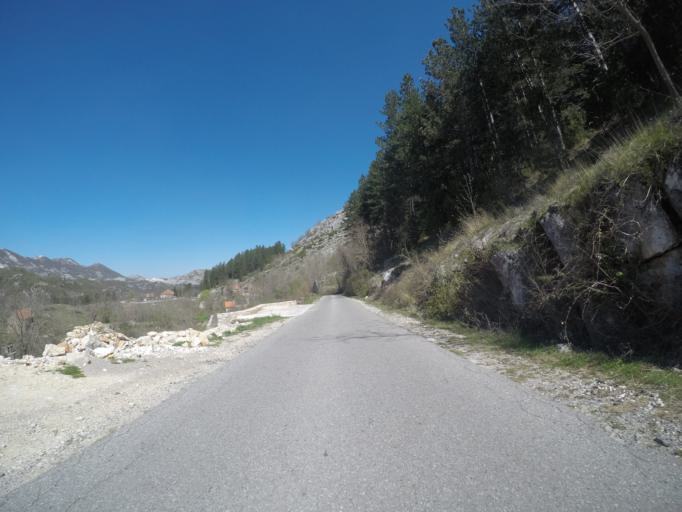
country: ME
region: Cetinje
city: Cetinje
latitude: 42.4624
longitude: 18.8633
